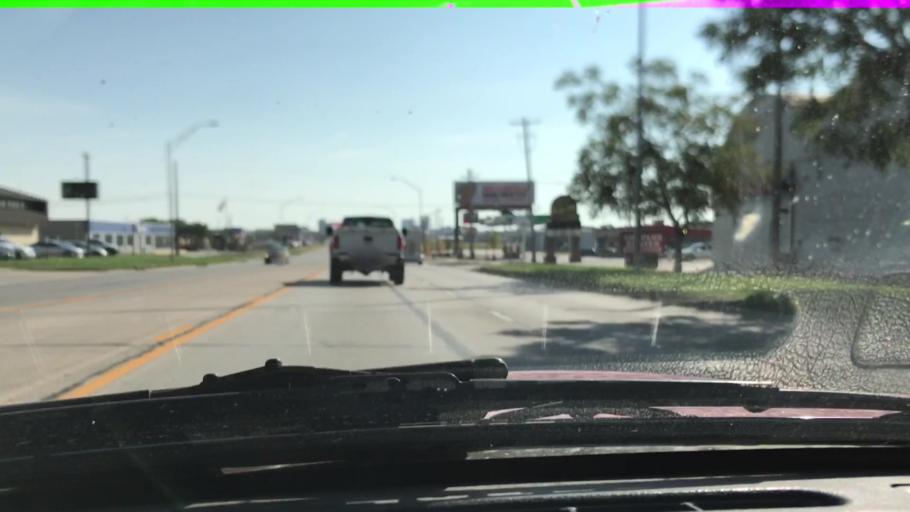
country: US
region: Nebraska
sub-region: Lancaster County
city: Lincoln
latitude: 40.8137
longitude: -96.7377
